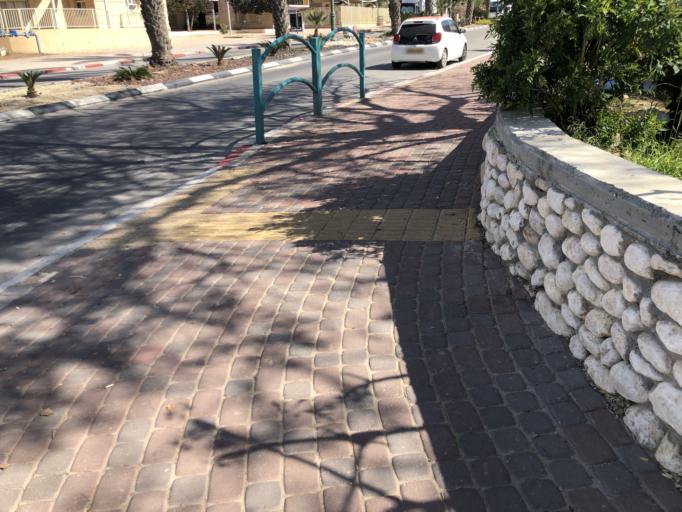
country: IL
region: Southern District
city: Dimona
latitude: 31.0670
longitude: 35.0373
